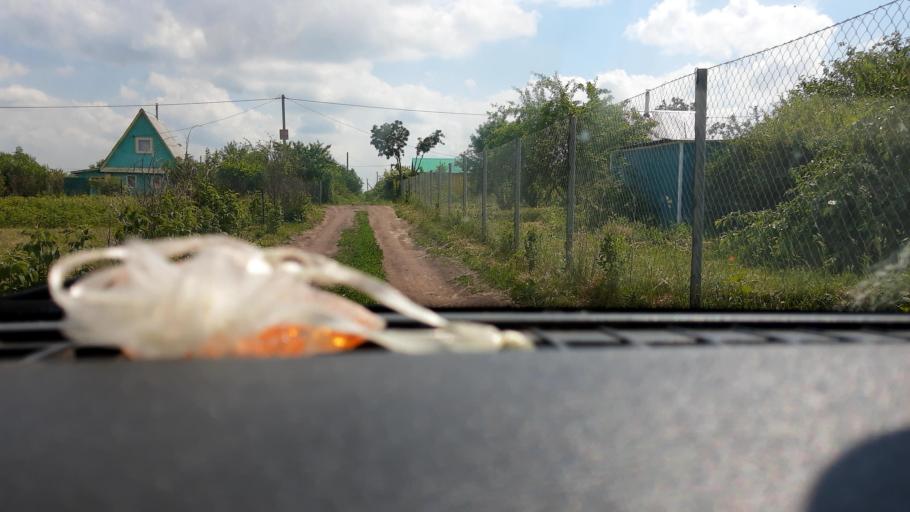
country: RU
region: Bashkortostan
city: Asanovo
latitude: 54.9177
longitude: 55.6345
